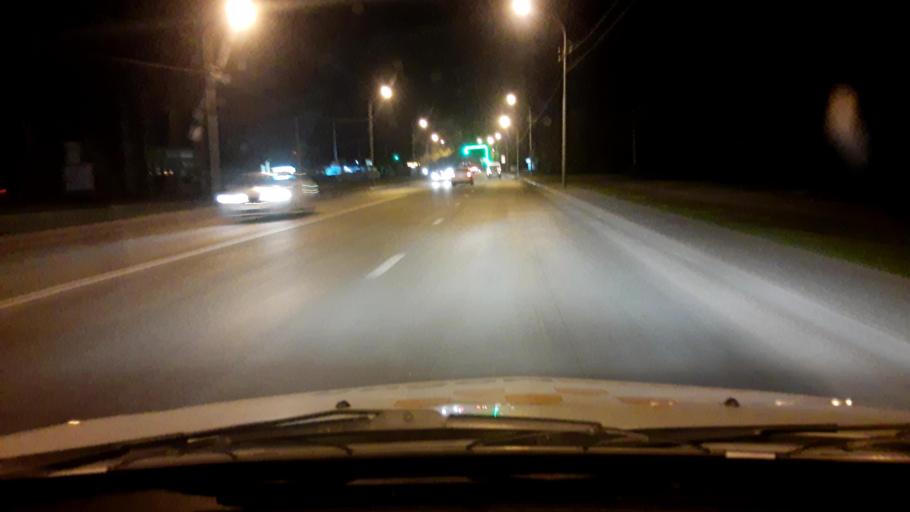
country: RU
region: Bashkortostan
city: Iglino
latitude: 54.7795
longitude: 56.2279
